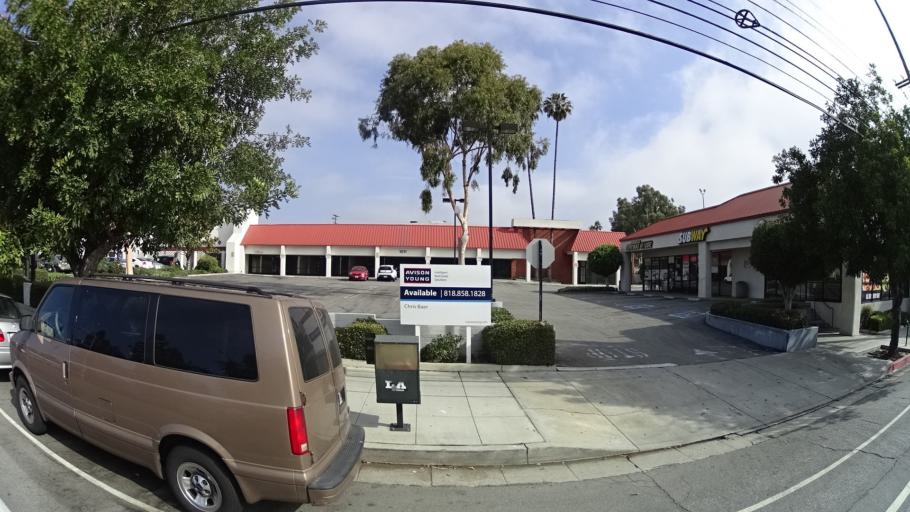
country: US
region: California
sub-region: Los Angeles County
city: Burbank
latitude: 34.1633
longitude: -118.3133
